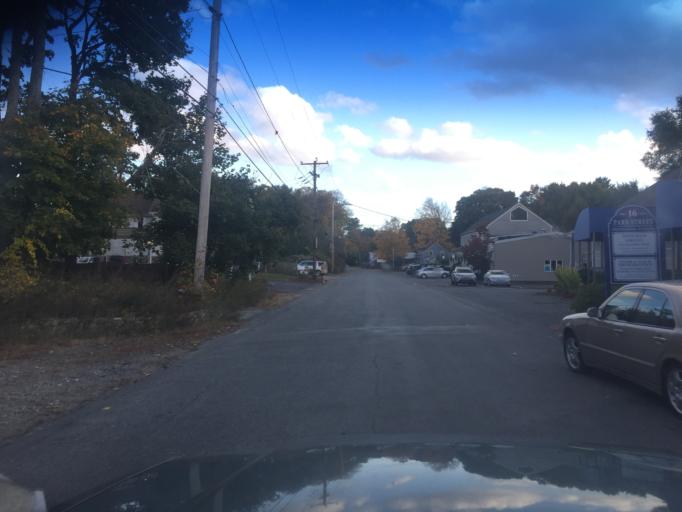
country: US
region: Massachusetts
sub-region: Norfolk County
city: Medfield
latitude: 42.1852
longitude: -71.3068
